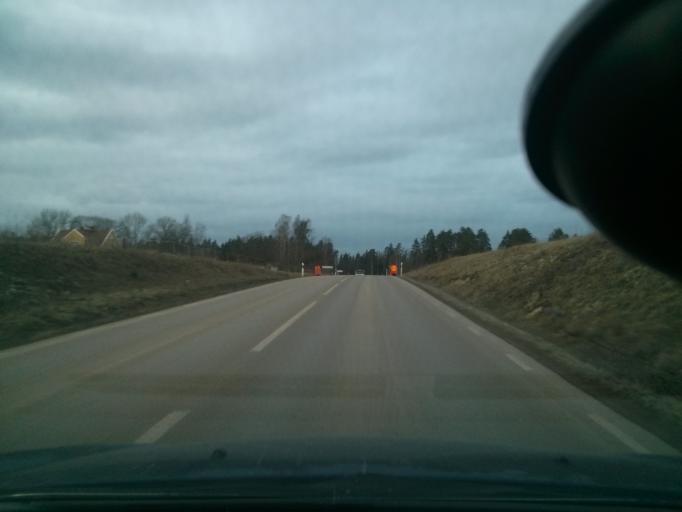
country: SE
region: Blekinge
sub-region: Ronneby Kommun
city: Brakne-Hoby
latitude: 56.3070
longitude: 15.1878
